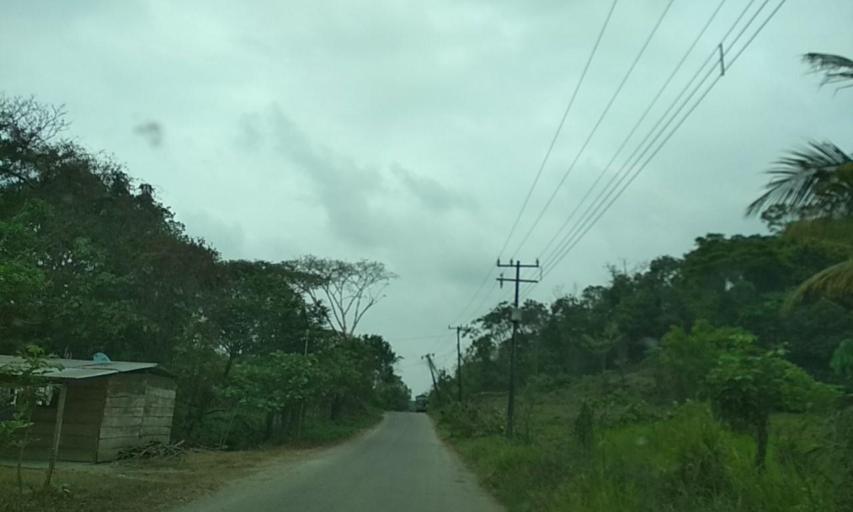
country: MX
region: Veracruz
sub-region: Uxpanapa
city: Poblado 10
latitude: 17.4622
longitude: -94.1064
